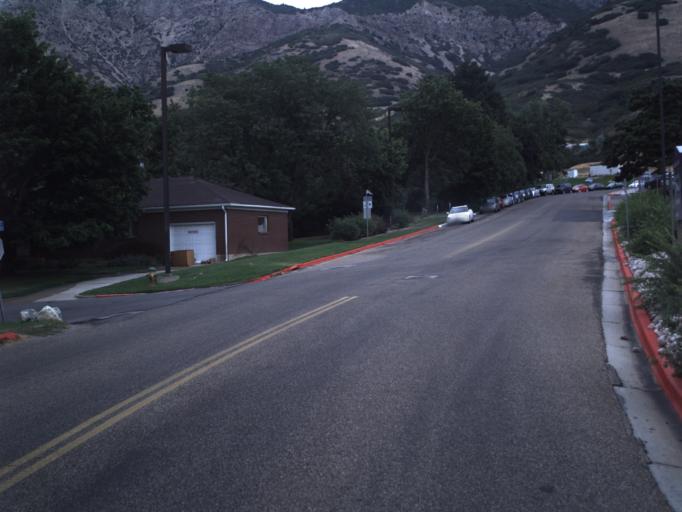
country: US
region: Utah
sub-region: Weber County
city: South Ogden
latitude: 41.1957
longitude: -111.9424
